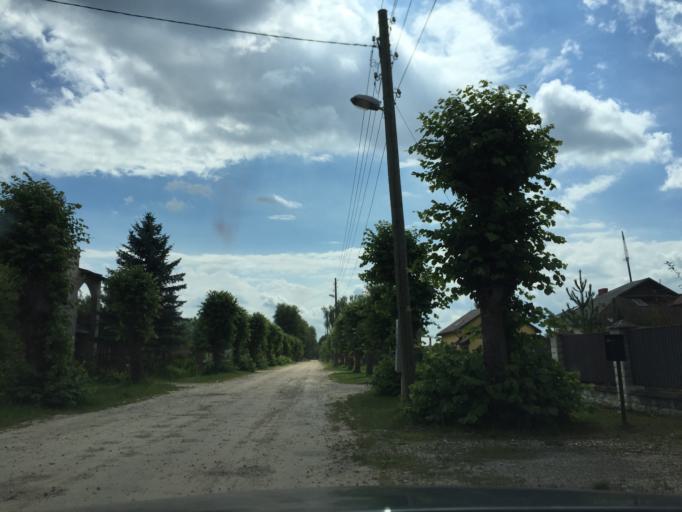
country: LV
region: Jelgava
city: Jelgava
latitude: 56.6503
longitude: 23.6798
